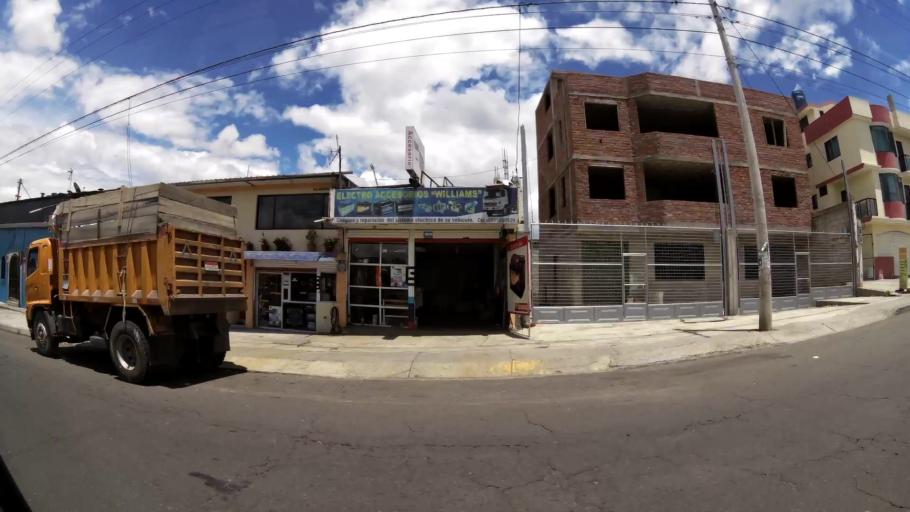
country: EC
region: Tungurahua
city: Ambato
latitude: -1.2922
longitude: -78.6043
